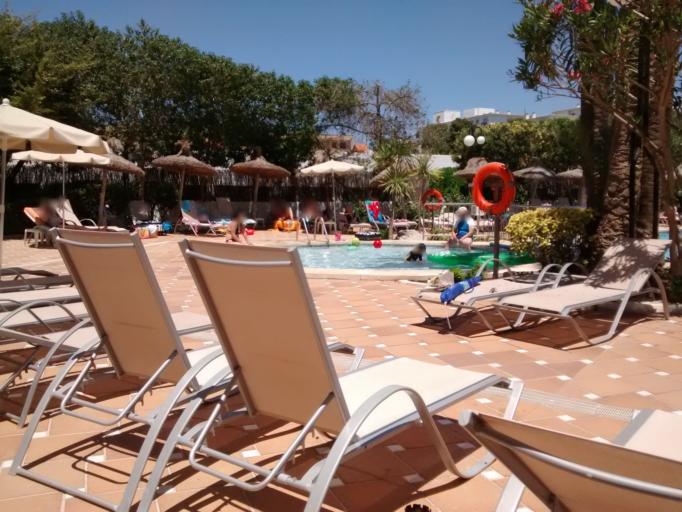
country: ES
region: Balearic Islands
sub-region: Illes Balears
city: Port d'Alcudia
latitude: 39.8102
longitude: 3.1152
